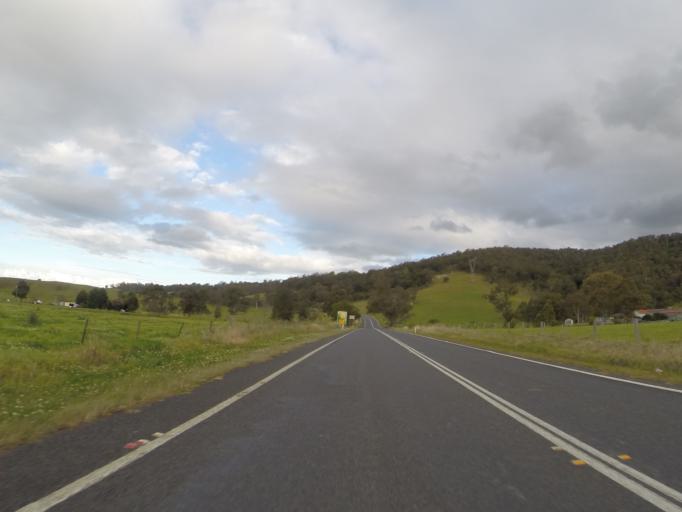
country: AU
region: New South Wales
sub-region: Shellharbour
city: Calderwood
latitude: -34.5817
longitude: 150.7153
